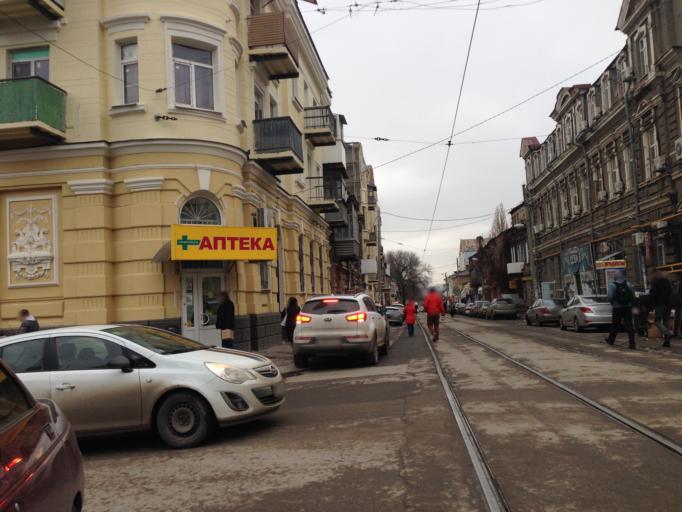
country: RU
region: Rostov
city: Rostov-na-Donu
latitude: 47.2187
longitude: 39.7173
